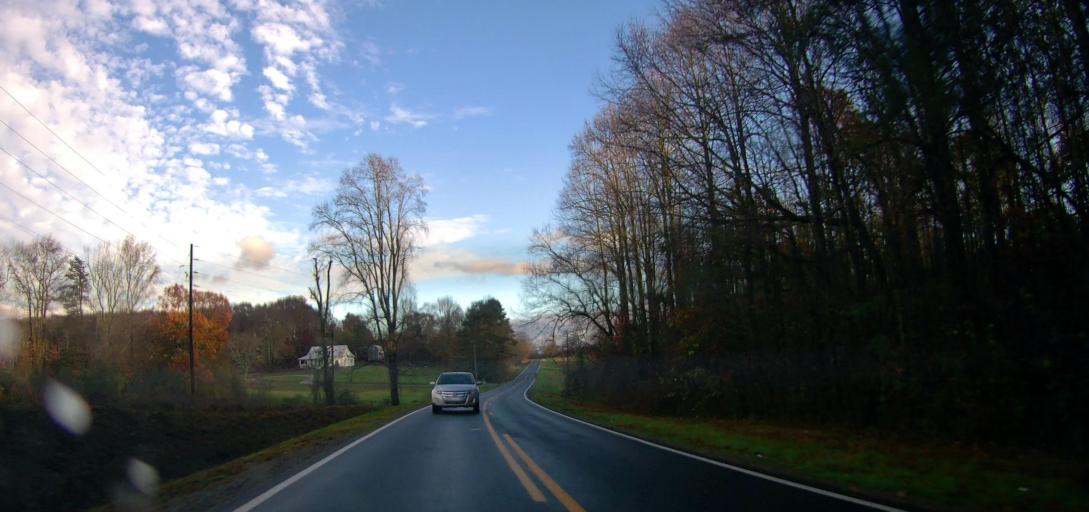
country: US
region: Georgia
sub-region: White County
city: Cleveland
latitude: 34.5727
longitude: -83.7453
